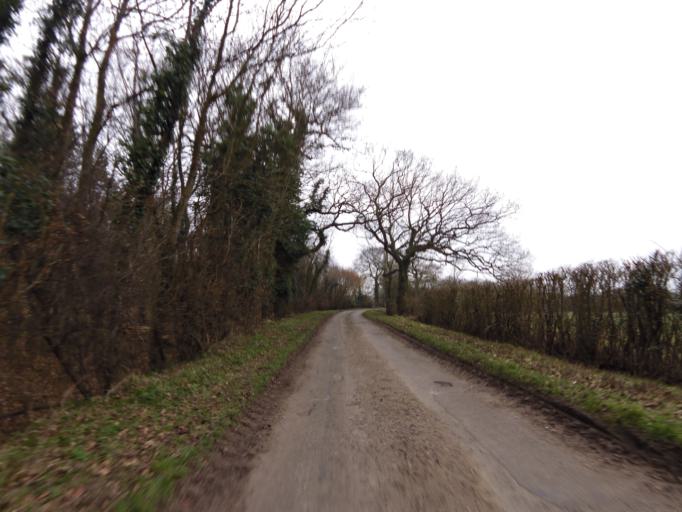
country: GB
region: England
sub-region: Suffolk
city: Cookley
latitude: 52.2522
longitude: 1.4119
